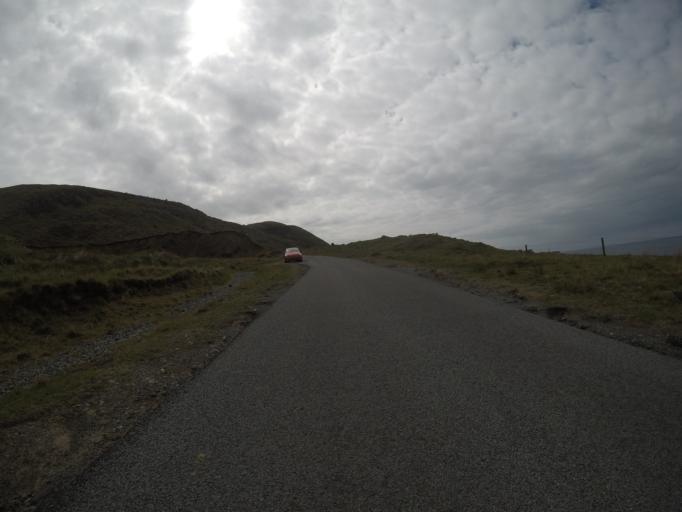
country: GB
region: Scotland
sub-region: Highland
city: Portree
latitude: 57.6703
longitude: -6.3532
